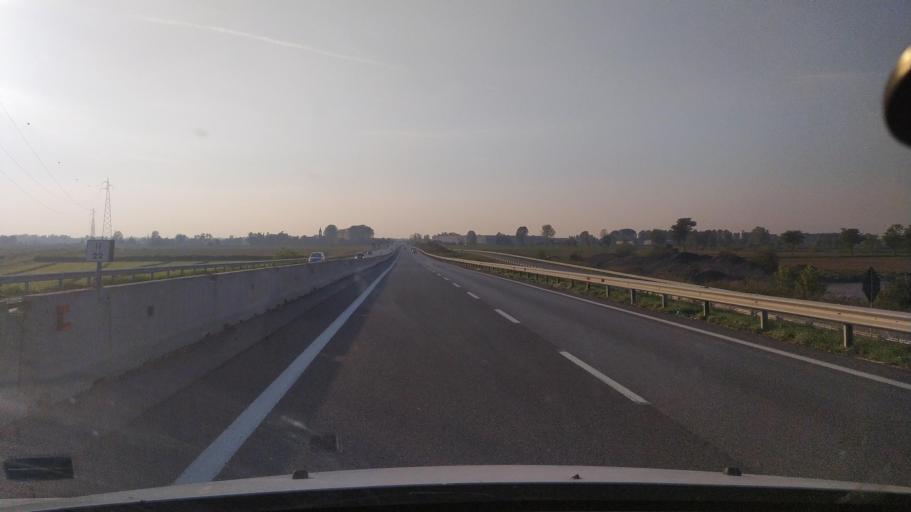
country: IT
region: Lombardy
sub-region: Provincia di Cremona
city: Nosadello
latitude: 45.3895
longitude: 9.5226
